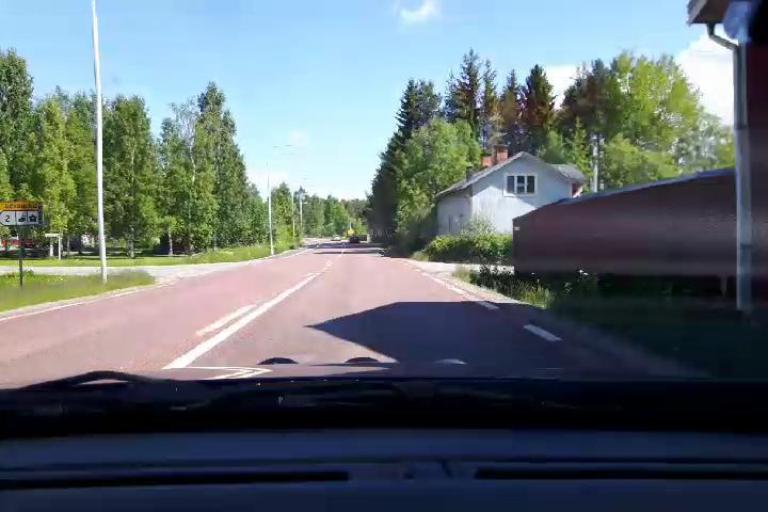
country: SE
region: Gaevleborg
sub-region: Hudiksvalls Kommun
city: Delsbo
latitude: 61.7868
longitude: 16.6111
